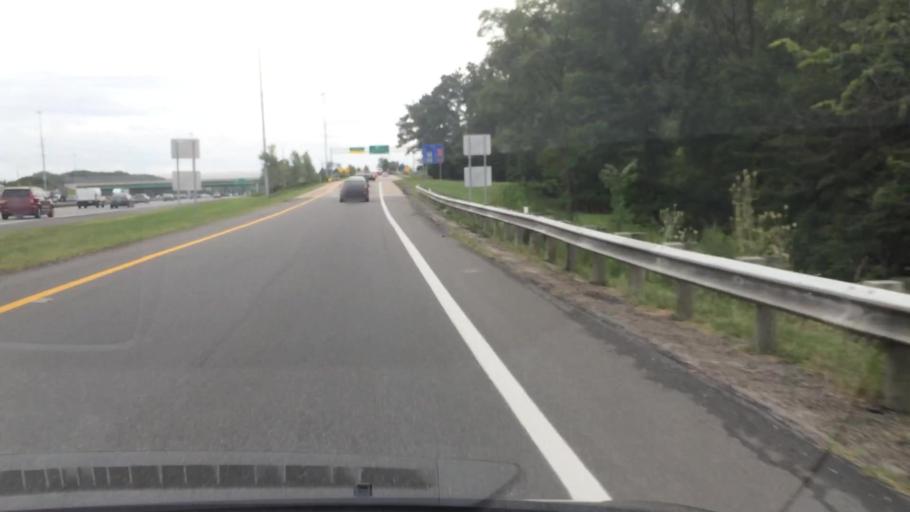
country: US
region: Ohio
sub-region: Cuyahoga County
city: Strongsville
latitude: 41.3171
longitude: -81.8129
